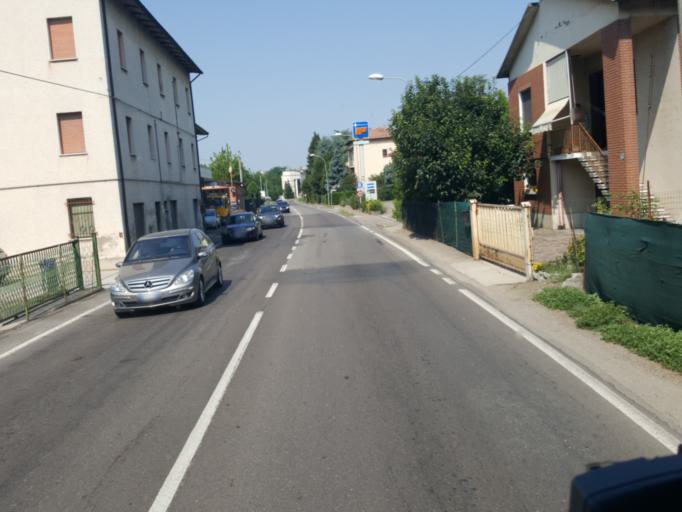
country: IT
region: Emilia-Romagna
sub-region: Provincia di Modena
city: Ca' di Sola
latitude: 44.5422
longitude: 10.9560
